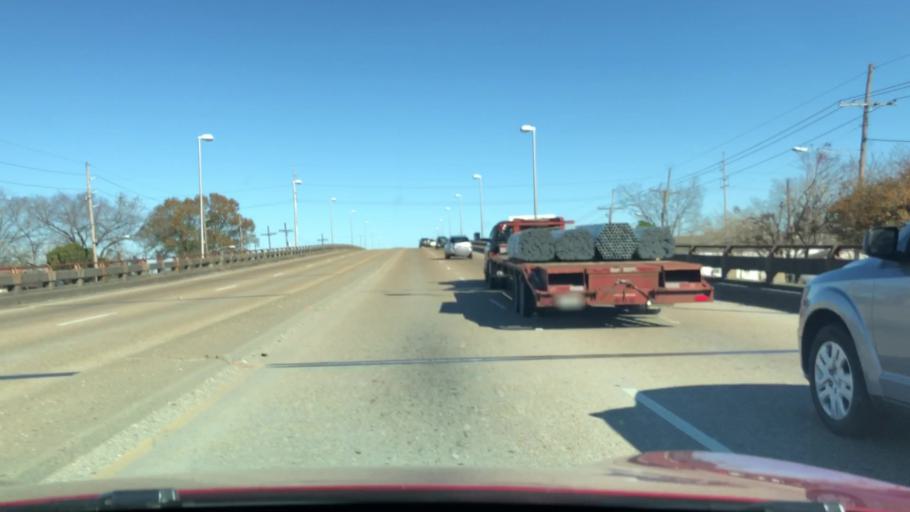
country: US
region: Louisiana
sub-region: Jefferson Parish
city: Jefferson
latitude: 29.9679
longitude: -90.1566
